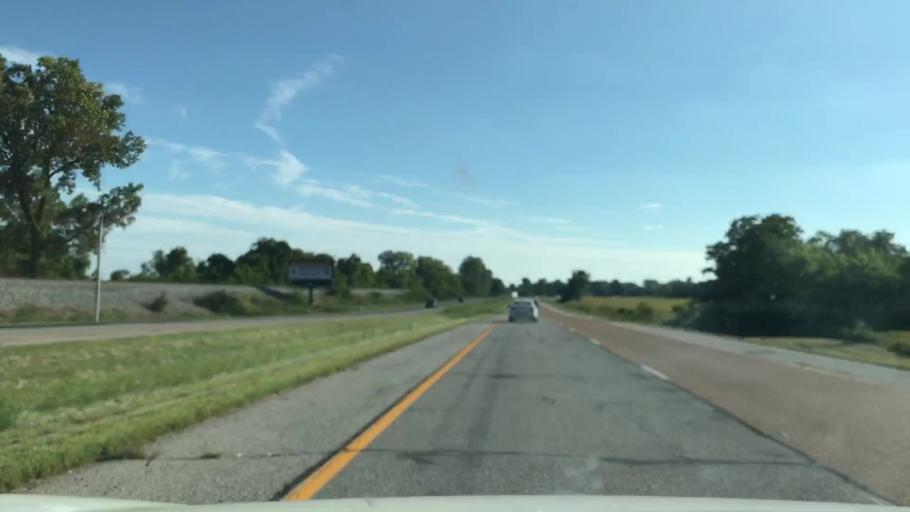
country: US
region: Illinois
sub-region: Madison County
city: Mitchell
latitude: 38.7869
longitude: -90.1066
